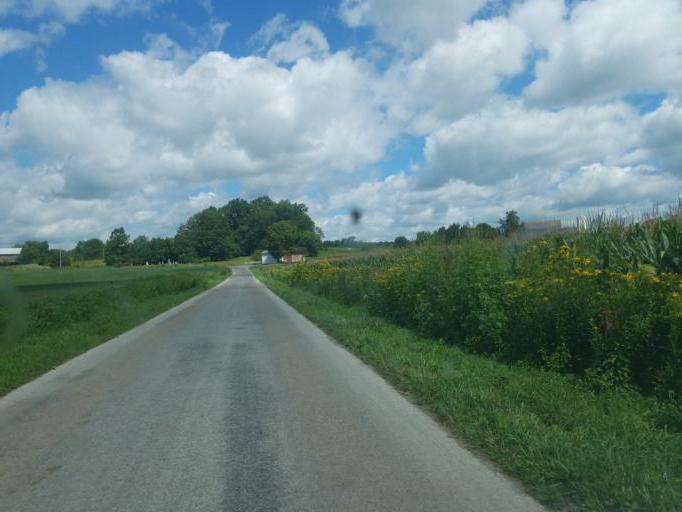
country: US
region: Ohio
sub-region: Knox County
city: Fredericktown
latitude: 40.5458
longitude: -82.6198
